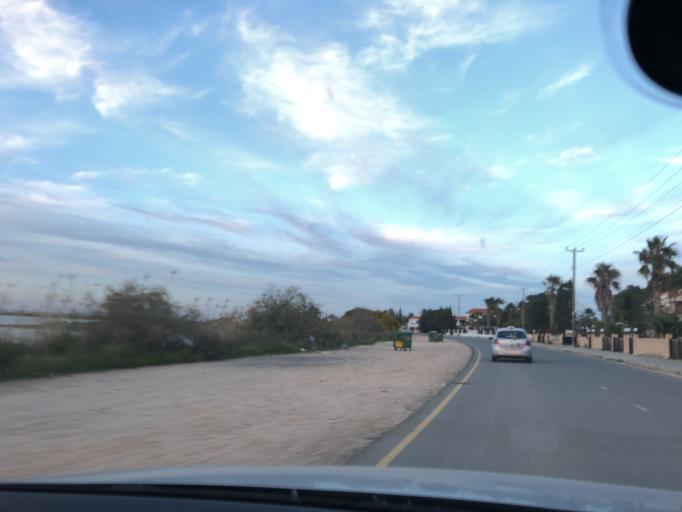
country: CY
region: Larnaka
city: Meneou
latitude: 34.8466
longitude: 33.6185
